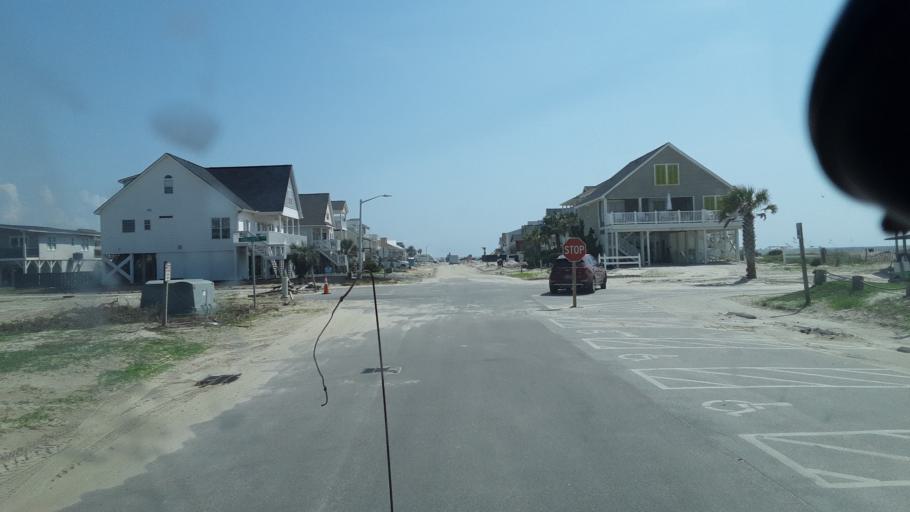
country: US
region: North Carolina
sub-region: Brunswick County
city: Shallotte
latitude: 33.8982
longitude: -78.3946
